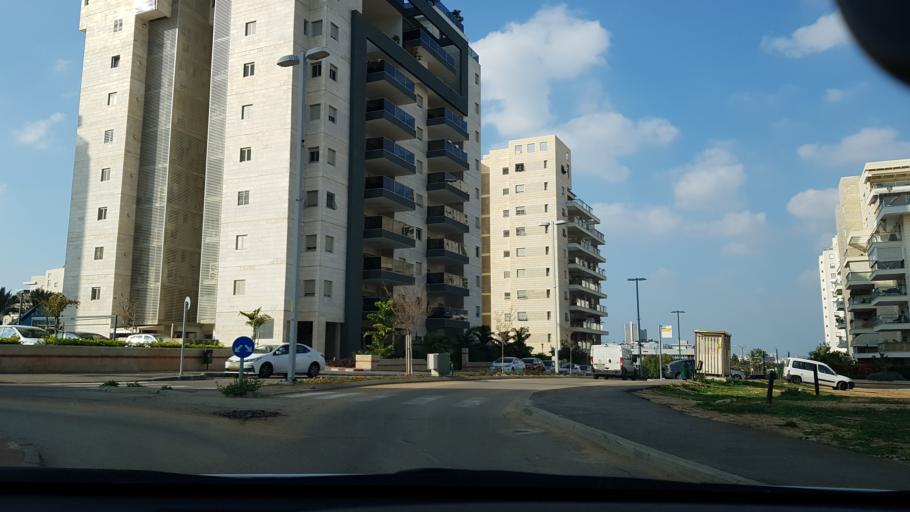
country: IL
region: Central District
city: Ness Ziona
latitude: 31.9038
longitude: 34.8215
